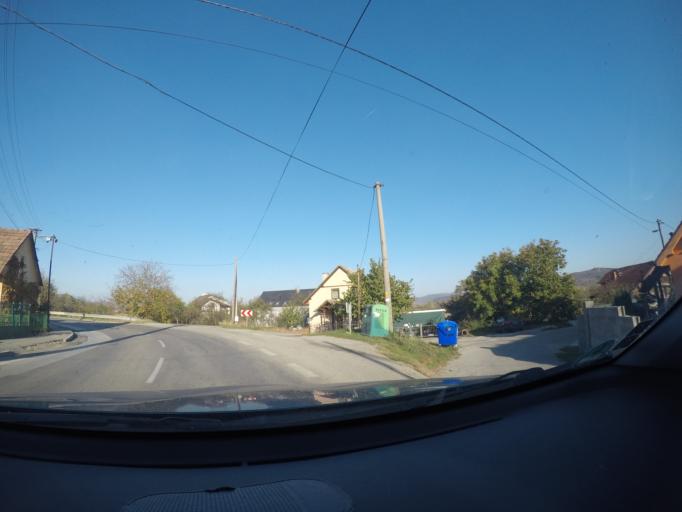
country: SK
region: Trenciansky
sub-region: Okres Trencin
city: Trencin
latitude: 48.9340
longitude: 18.0753
